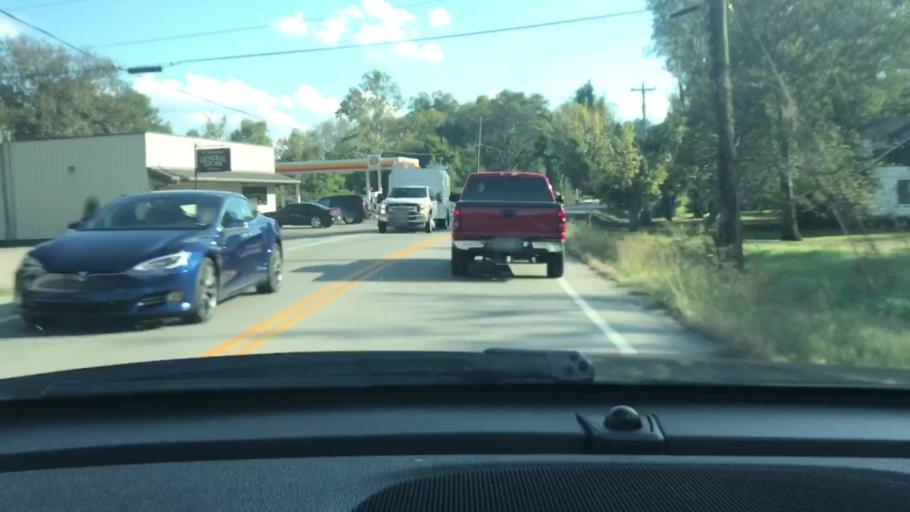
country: US
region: Tennessee
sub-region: Sumner County
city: Shackle Island
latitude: 36.3738
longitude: -86.6171
